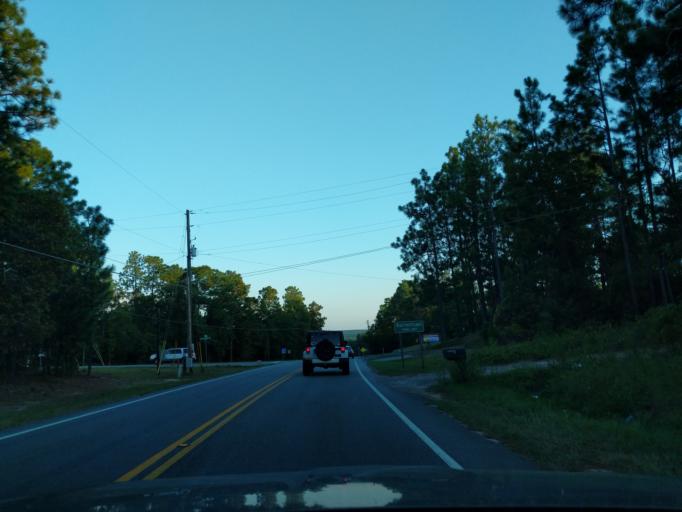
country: US
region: South Carolina
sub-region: Aiken County
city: Burnettown
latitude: 33.5351
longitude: -81.8620
